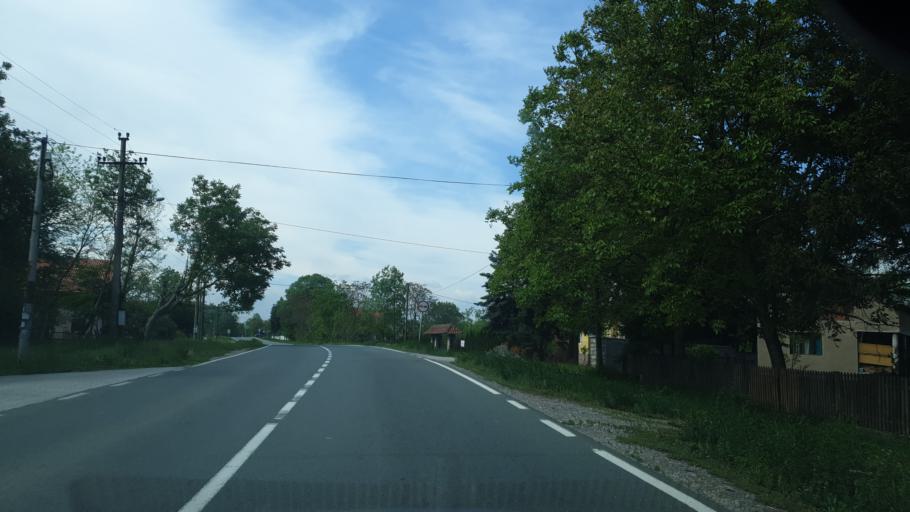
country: RS
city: Stubline
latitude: 44.5907
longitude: 20.1482
